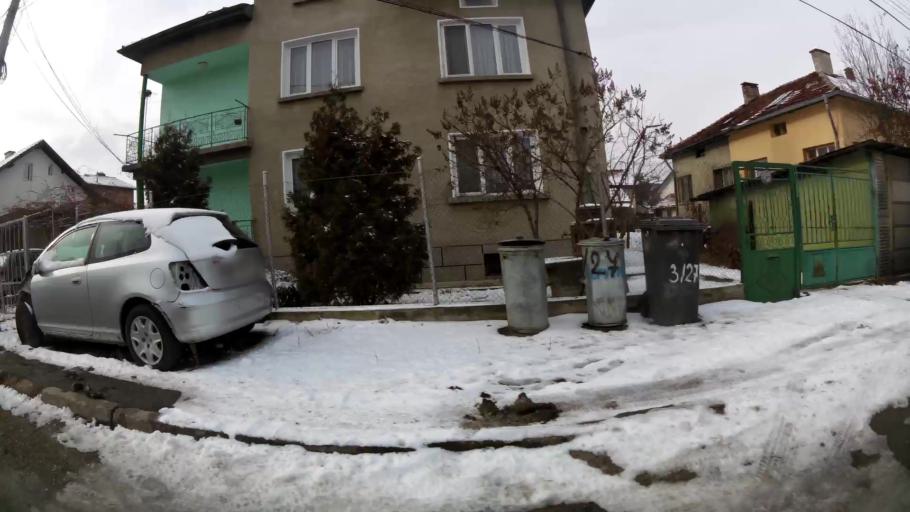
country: BG
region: Sofia-Capital
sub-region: Stolichna Obshtina
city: Sofia
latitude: 42.7098
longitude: 23.4042
